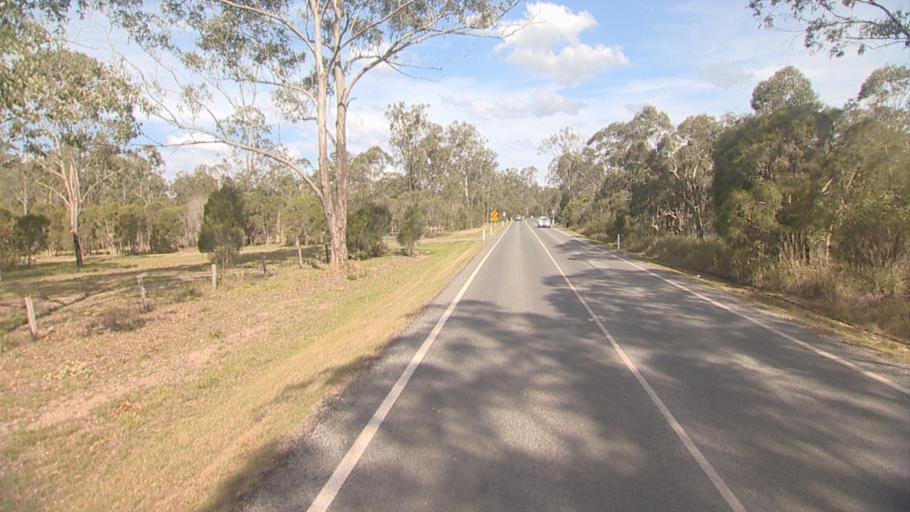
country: AU
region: Queensland
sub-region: Logan
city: Cedar Vale
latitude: -27.8291
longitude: 153.0383
